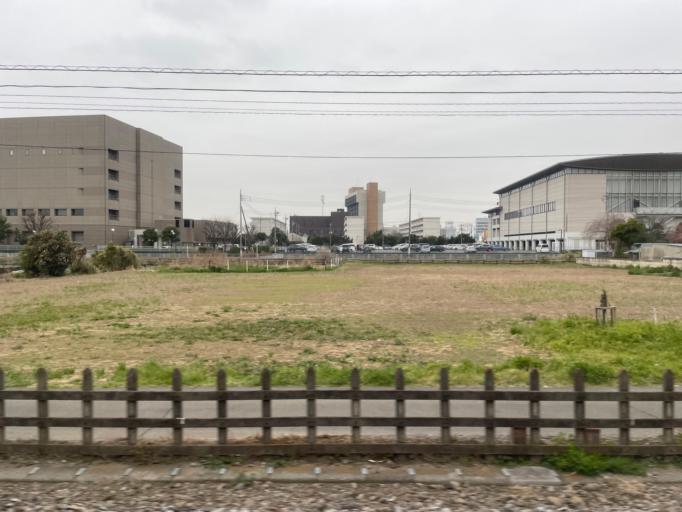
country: JP
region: Gunma
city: Maebashi-shi
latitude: 36.3859
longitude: 139.0523
